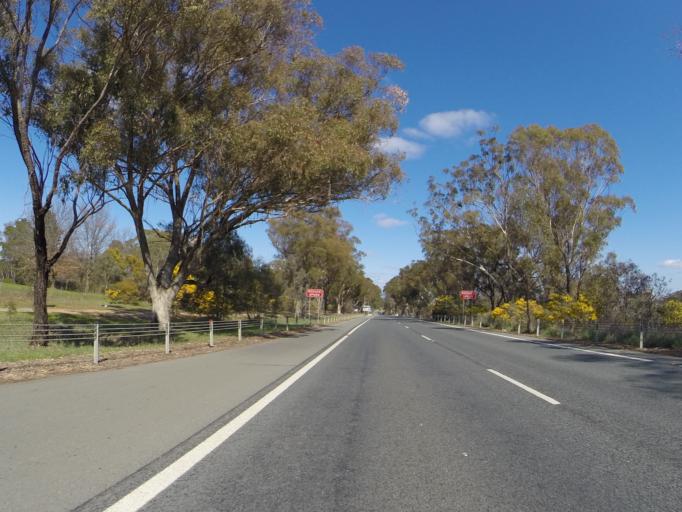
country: AU
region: Australian Capital Territory
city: Kaleen
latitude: -35.2229
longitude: 149.1714
